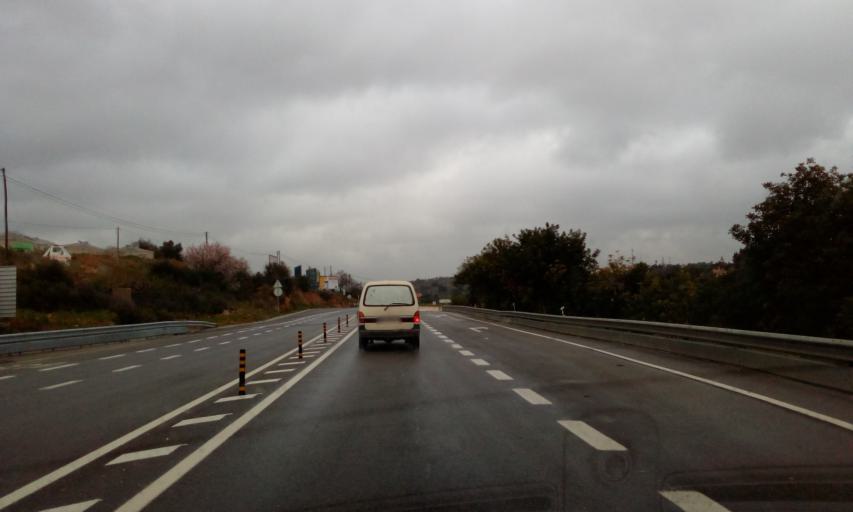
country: PT
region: Faro
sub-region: Albufeira
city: Guia
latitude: 37.1261
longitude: -8.3167
